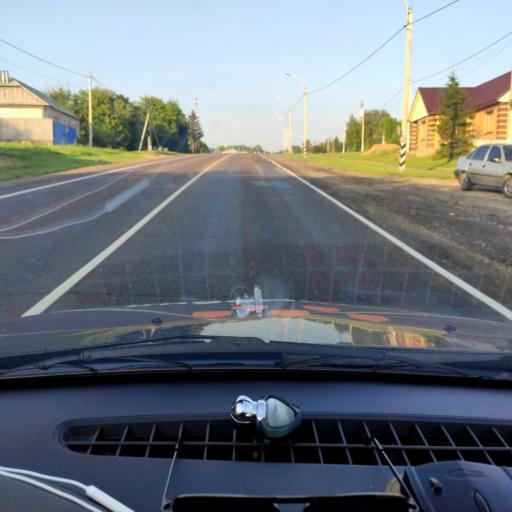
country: RU
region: Lipetsk
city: Kazaki
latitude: 52.6206
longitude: 38.2685
